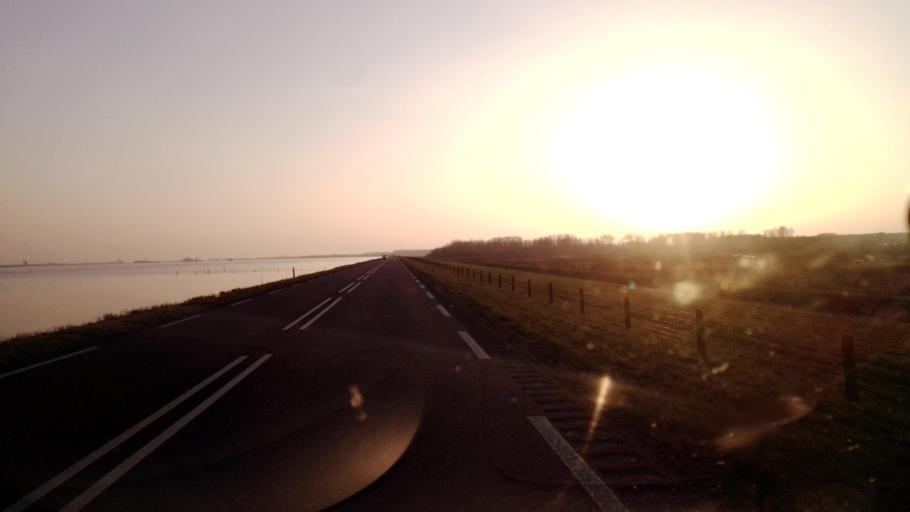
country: NL
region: Flevoland
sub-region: Gemeente Dronten
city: Biddinghuizen
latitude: 52.4068
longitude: 5.6898
